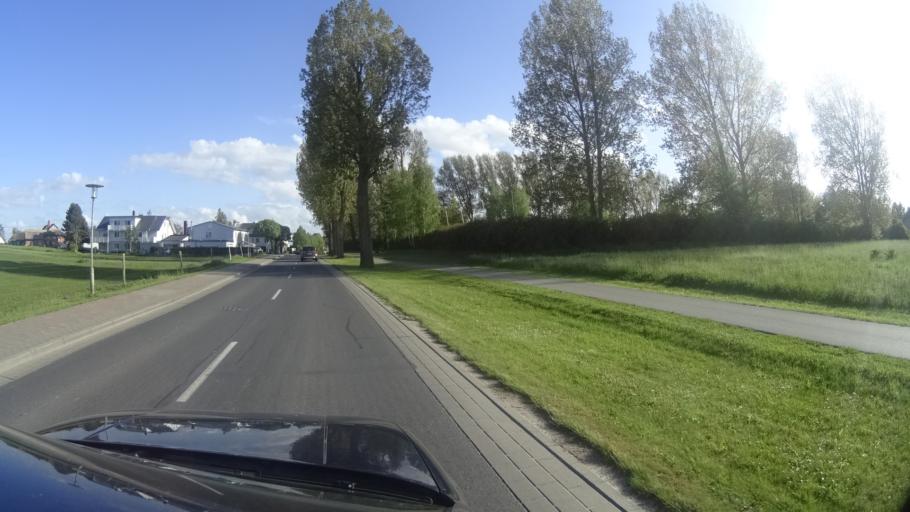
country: DE
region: Mecklenburg-Vorpommern
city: Ostseebad Dierhagen
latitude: 54.3768
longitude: 12.4160
